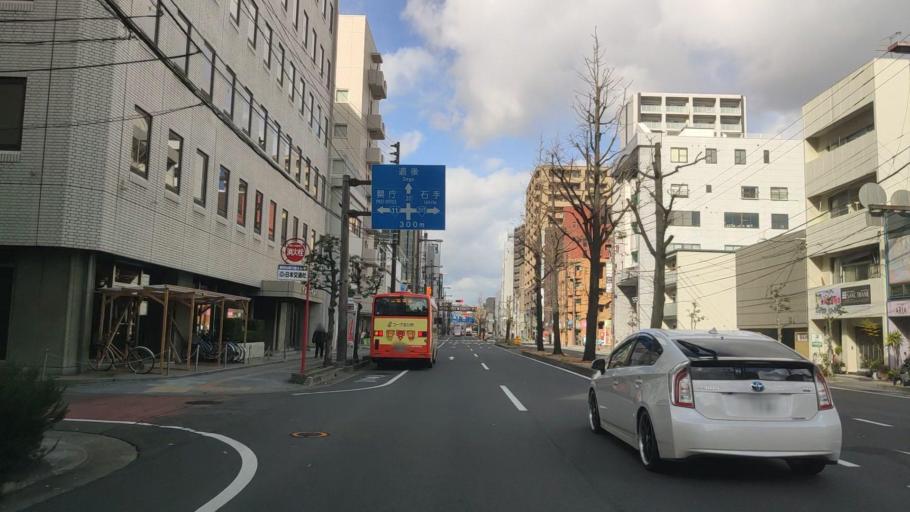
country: JP
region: Ehime
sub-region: Shikoku-chuo Shi
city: Matsuyama
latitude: 33.8390
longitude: 132.7753
